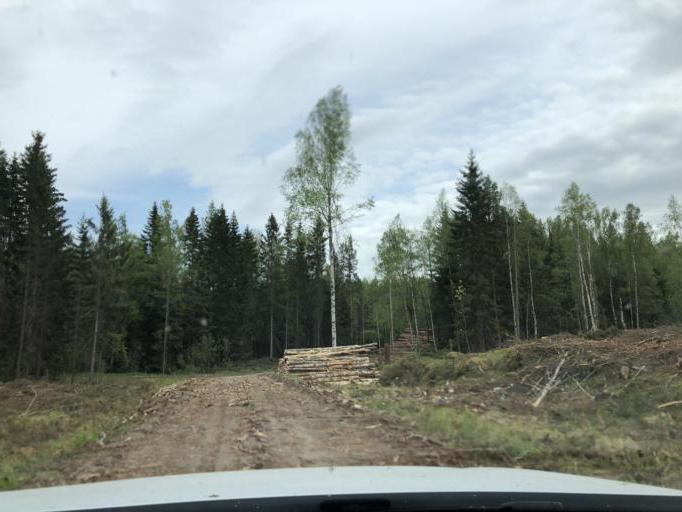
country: SE
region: Uppsala
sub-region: Heby Kommun
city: OEstervala
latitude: 60.3746
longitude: 17.2310
